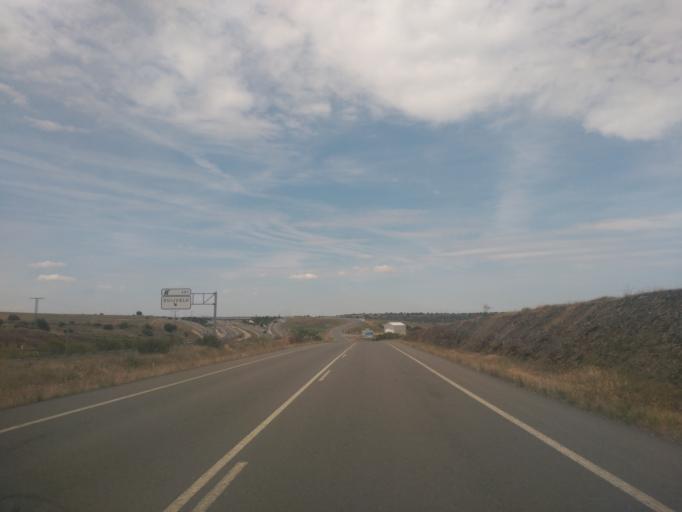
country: ES
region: Castille and Leon
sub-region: Provincia de Salamanca
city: Guijuelo
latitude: 40.5667
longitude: -5.6588
